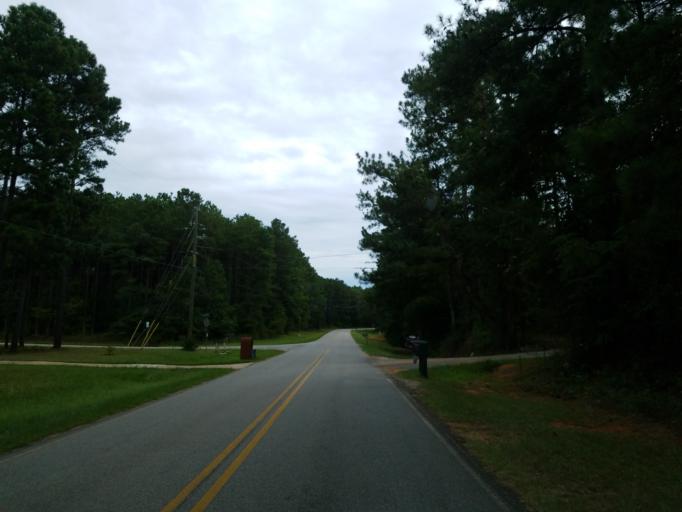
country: US
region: Georgia
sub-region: Monroe County
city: Forsyth
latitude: 32.9410
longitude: -83.9388
